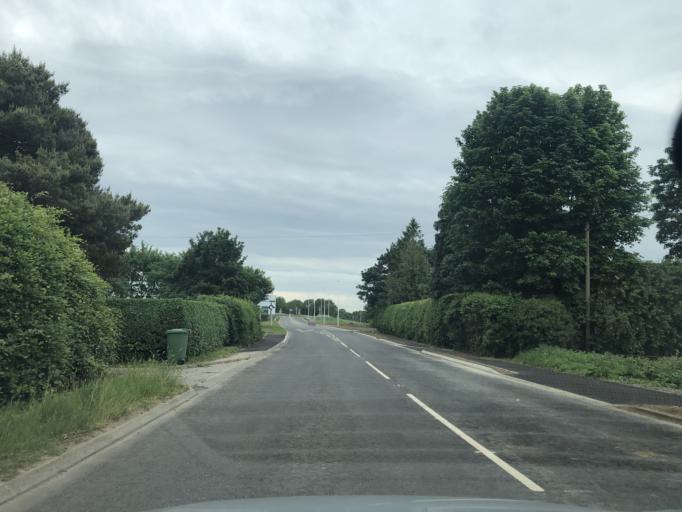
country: GB
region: England
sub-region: North Yorkshire
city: Thirsk
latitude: 54.2083
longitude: -1.3588
